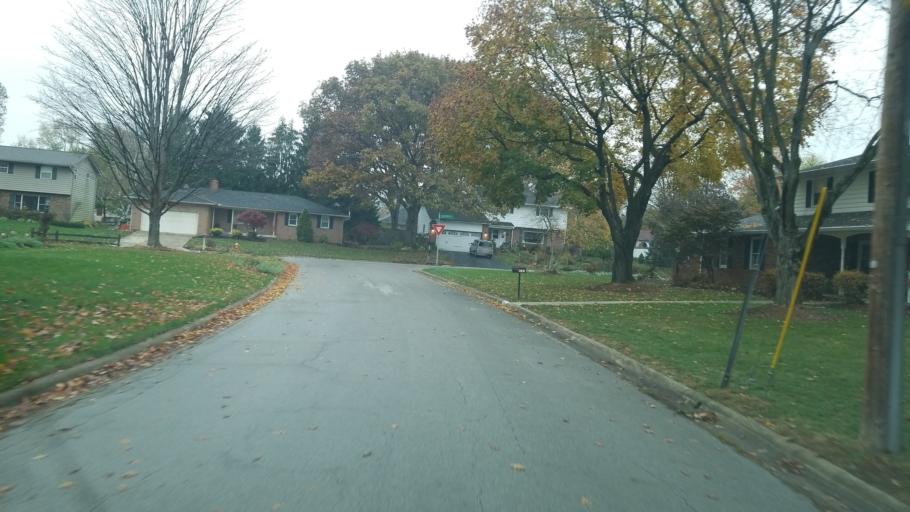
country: US
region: Ohio
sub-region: Franklin County
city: Worthington
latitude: 40.0800
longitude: -83.0455
